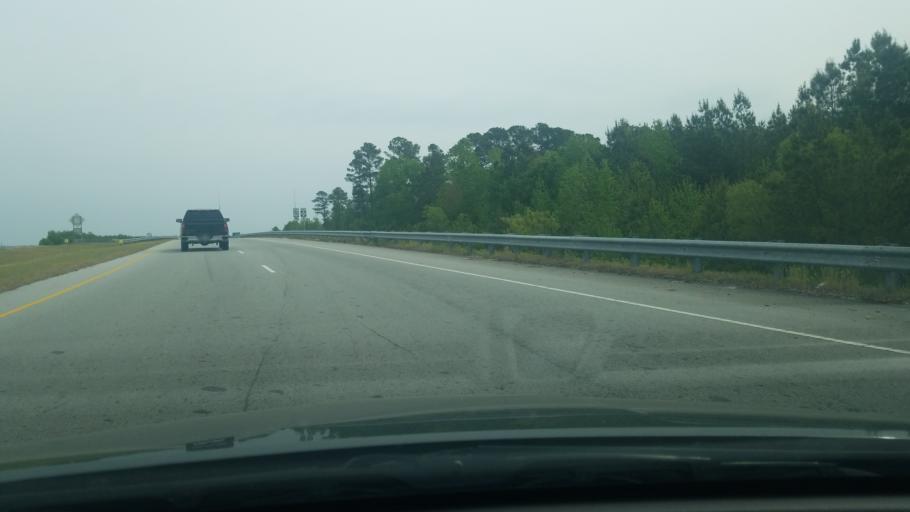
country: US
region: North Carolina
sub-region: Craven County
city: River Bend
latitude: 35.1256
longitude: -77.1347
